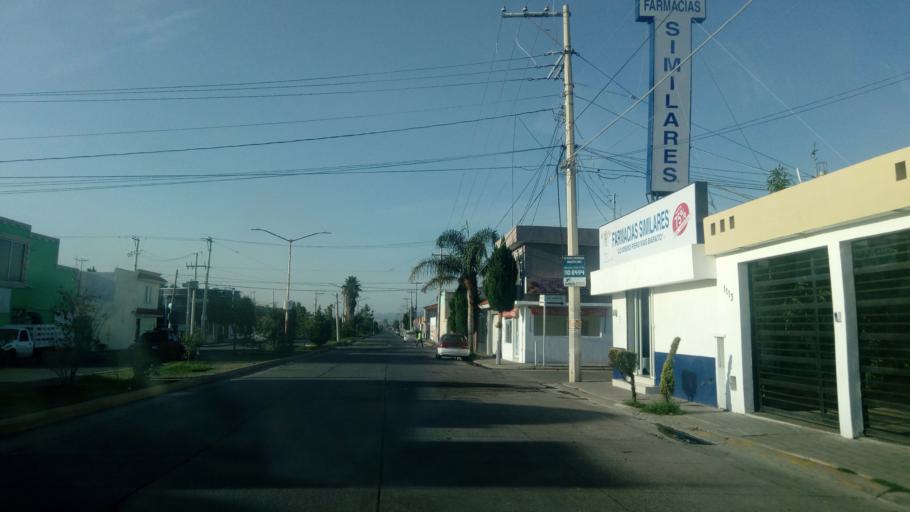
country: MX
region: Durango
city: Victoria de Durango
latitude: 24.0725
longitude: -104.5874
